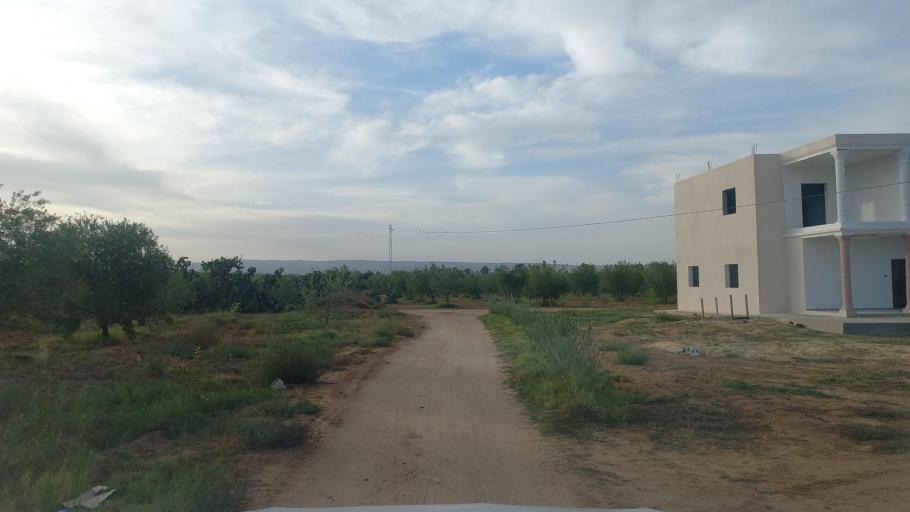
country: TN
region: Al Qasrayn
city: Kasserine
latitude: 35.2522
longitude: 9.0390
